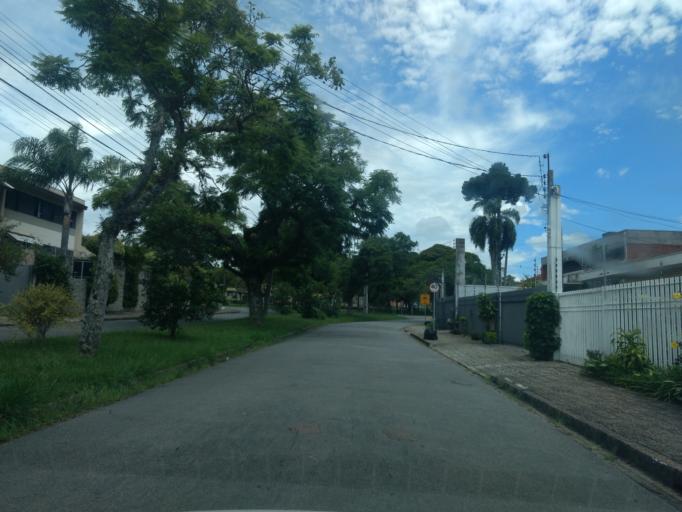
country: BR
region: Parana
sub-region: Curitiba
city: Curitiba
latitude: -25.4196
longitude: -49.2320
